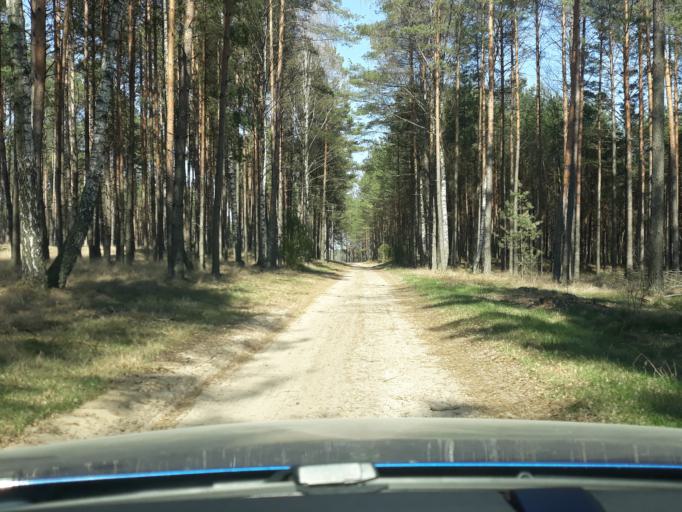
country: PL
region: Pomeranian Voivodeship
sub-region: Powiat bytowski
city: Lipnica
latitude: 53.8683
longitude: 17.4320
